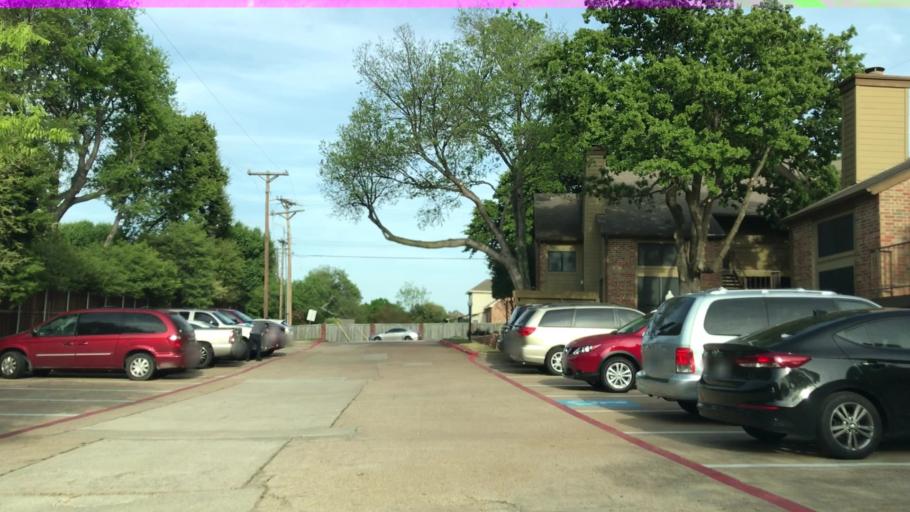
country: US
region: Texas
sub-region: Tarrant County
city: Grapevine
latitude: 32.9473
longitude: -97.1000
